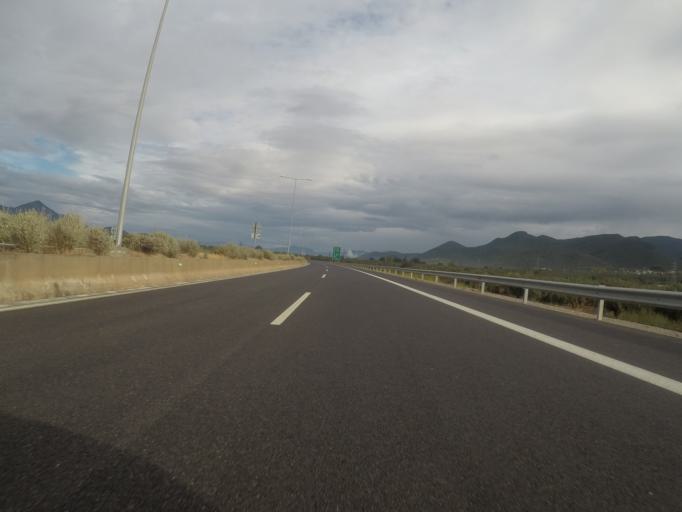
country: GR
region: Peloponnese
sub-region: Nomos Messinias
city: Arfara
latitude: 37.1445
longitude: 22.0358
